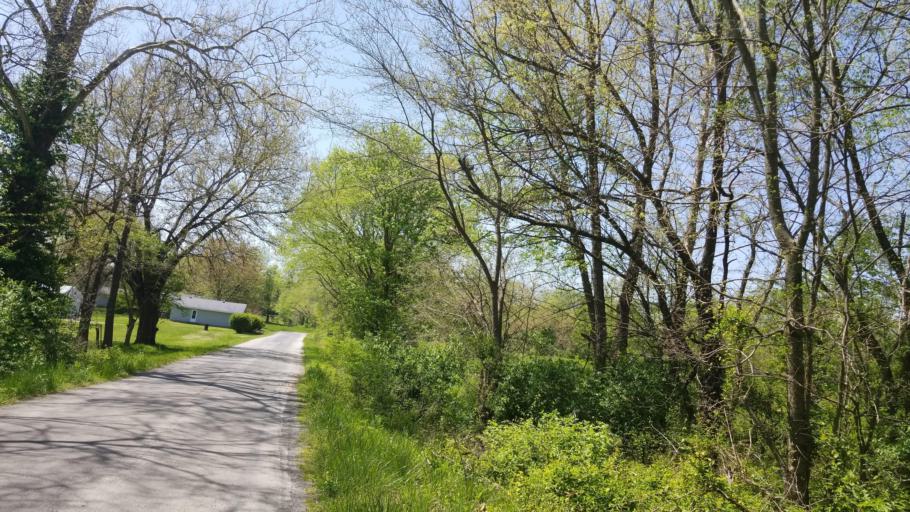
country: US
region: Illinois
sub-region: Saline County
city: Harrisburg
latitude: 37.8468
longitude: -88.6033
